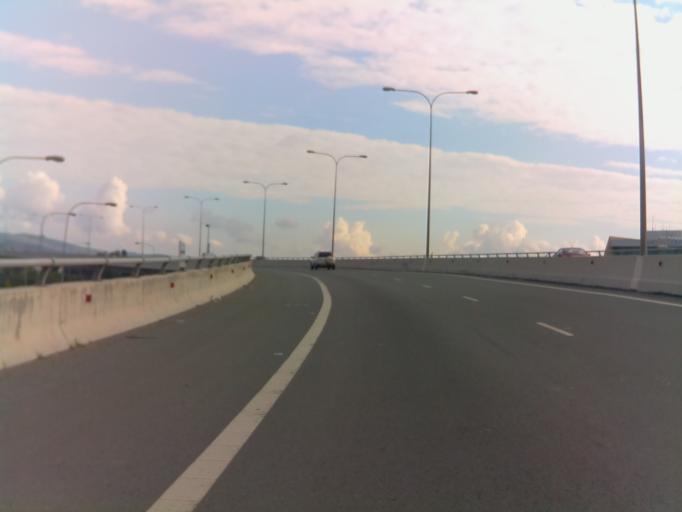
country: CY
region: Limassol
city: Pano Polemidia
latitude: 34.6885
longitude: 33.0083
